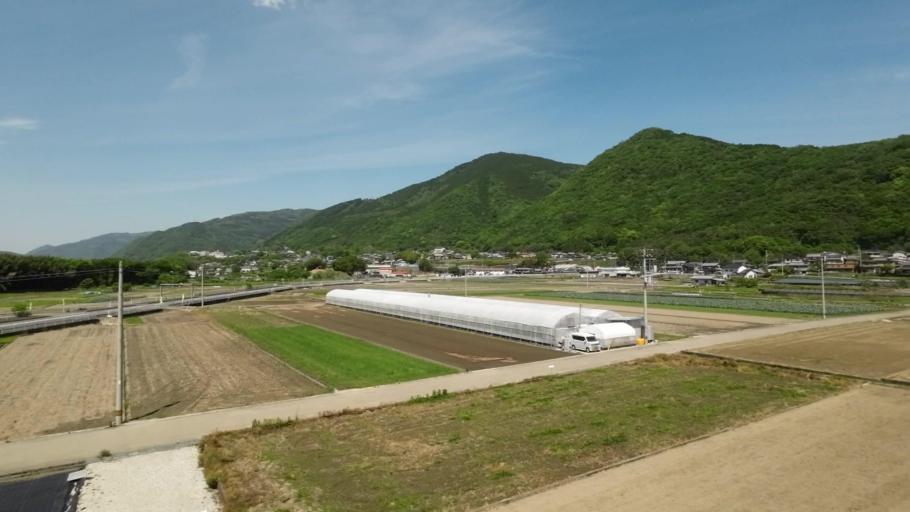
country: JP
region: Tokushima
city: Ikedacho
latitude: 34.0386
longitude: 133.8655
